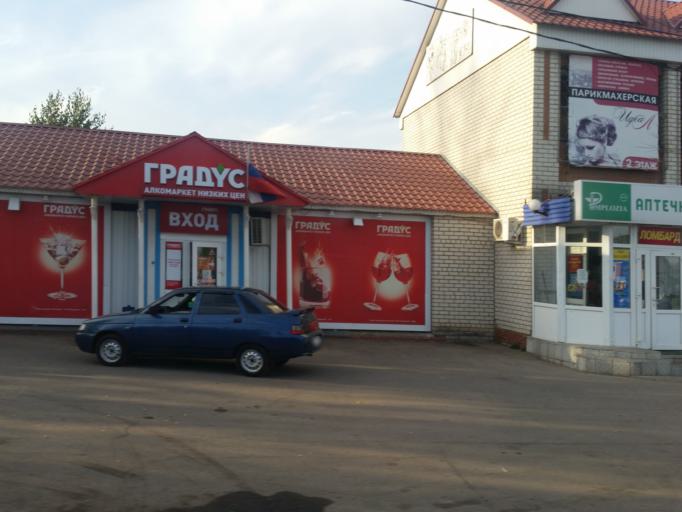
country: RU
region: Ulyanovsk
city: Cherdakly
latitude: 54.3557
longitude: 48.8539
